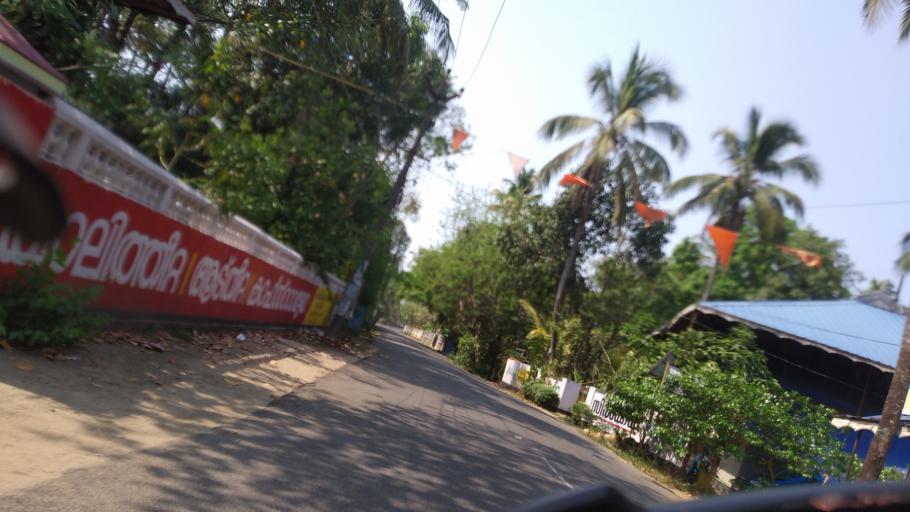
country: IN
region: Kerala
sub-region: Thrissur District
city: Thanniyam
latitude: 10.3301
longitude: 76.1215
